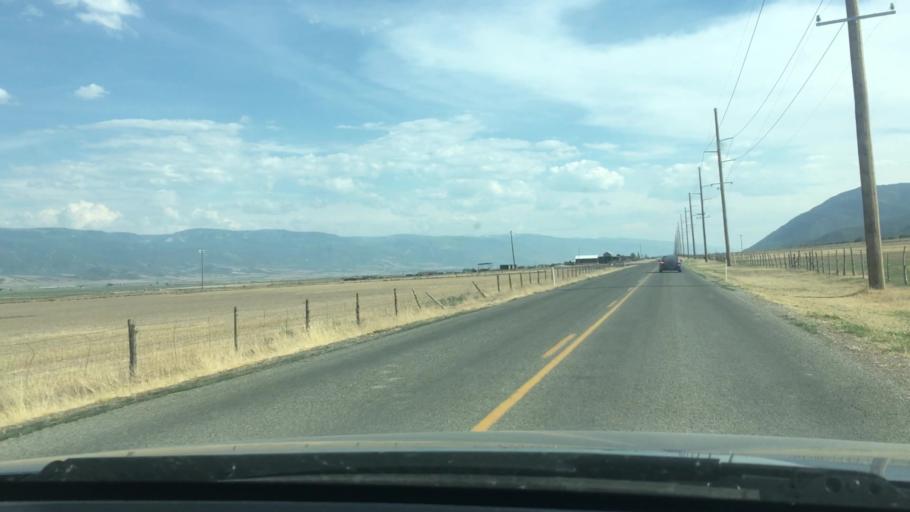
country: US
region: Utah
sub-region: Sanpete County
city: Moroni
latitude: 39.5254
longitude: -111.6397
